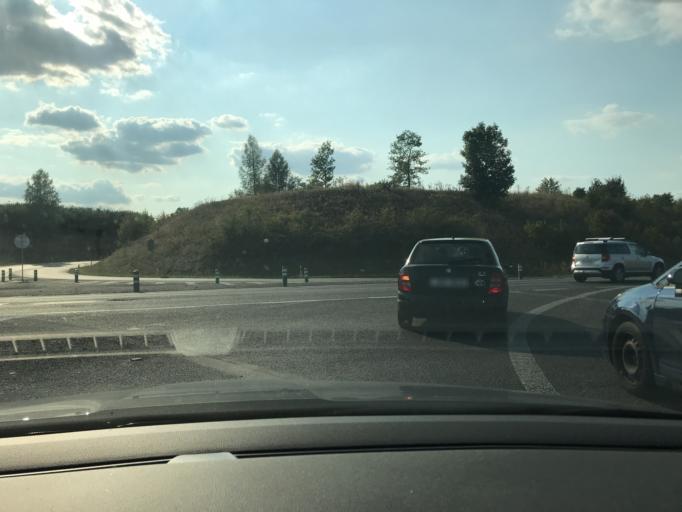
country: CZ
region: Central Bohemia
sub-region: Okres Kladno
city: Slany
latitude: 50.2328
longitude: 14.0545
